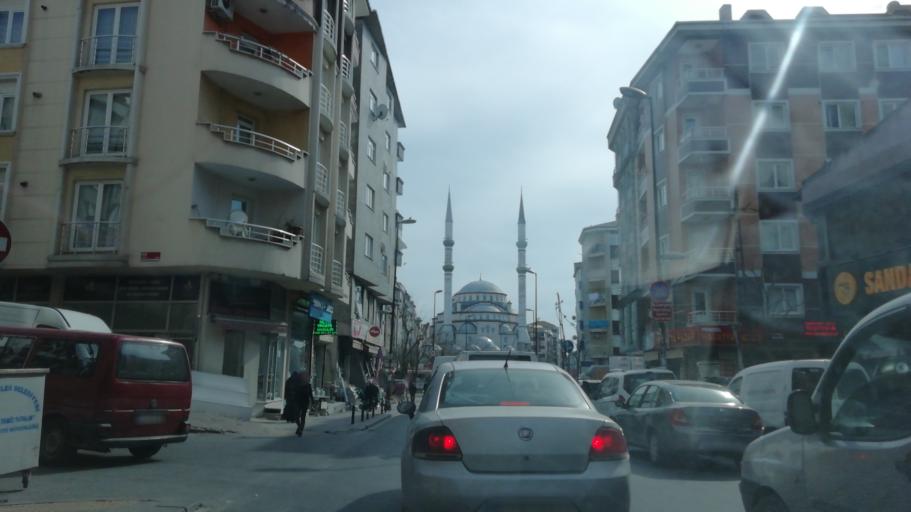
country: TR
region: Istanbul
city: Bahcelievler
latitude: 41.0112
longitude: 28.8390
